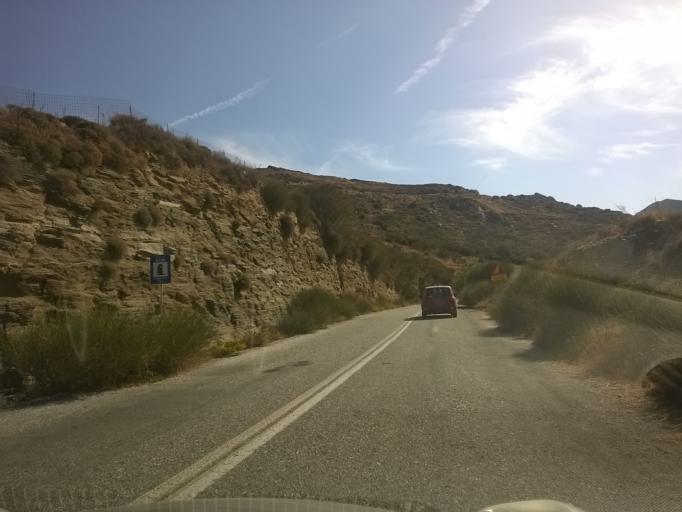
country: GR
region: South Aegean
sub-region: Nomos Kykladon
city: Filotion
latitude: 37.1585
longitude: 25.5537
